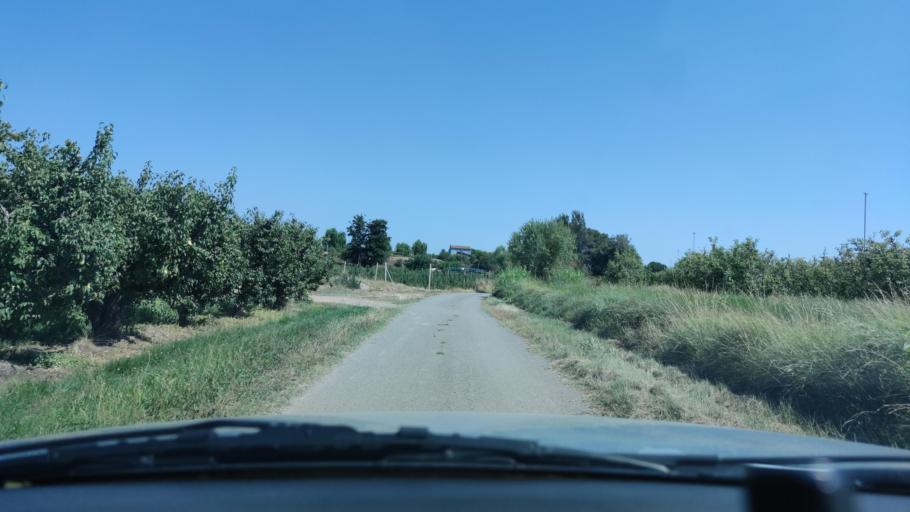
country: ES
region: Catalonia
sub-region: Provincia de Lleida
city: Alcoletge
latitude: 41.6684
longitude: 0.6619
